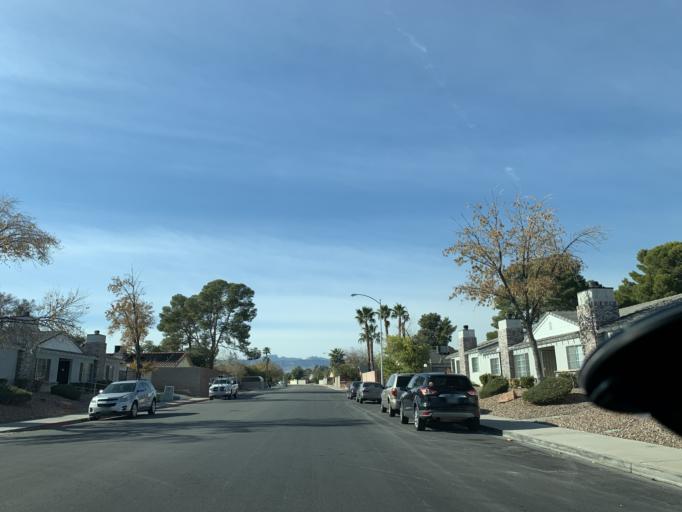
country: US
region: Nevada
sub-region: Clark County
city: Spring Valley
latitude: 36.1056
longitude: -115.2255
